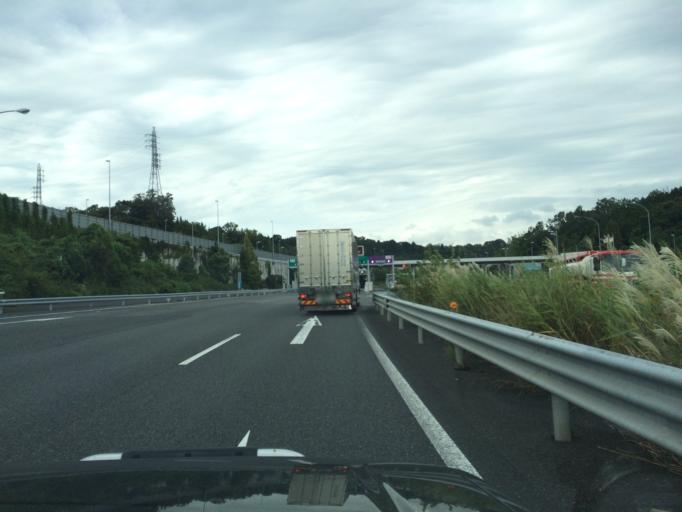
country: JP
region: Mie
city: Kameyama
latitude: 34.8599
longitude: 136.4134
